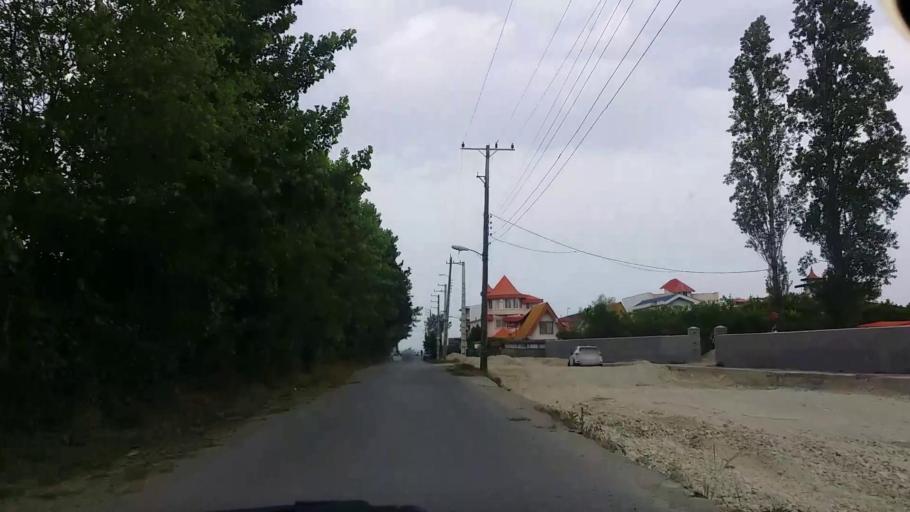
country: IR
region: Mazandaran
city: Chalus
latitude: 36.6837
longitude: 51.4033
